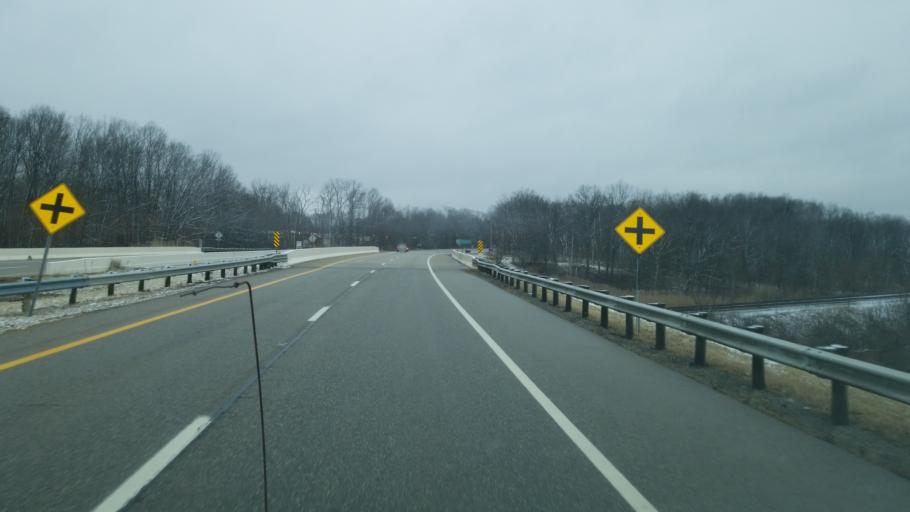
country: US
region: Ohio
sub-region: Portage County
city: Ravenna
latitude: 41.1474
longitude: -81.2225
